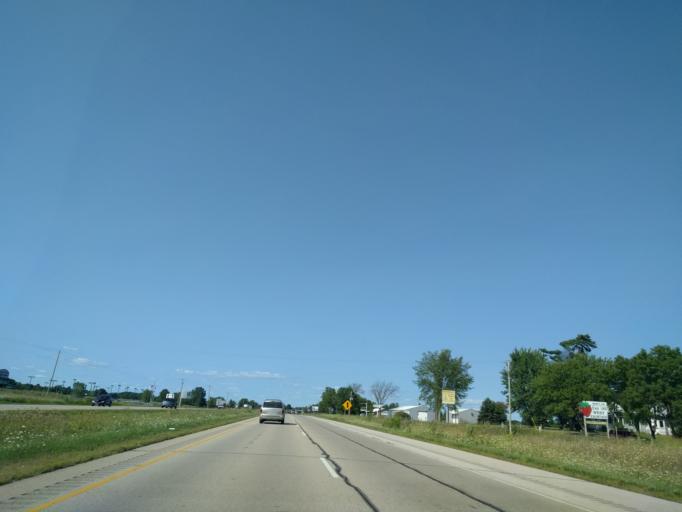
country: US
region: Wisconsin
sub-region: Brown County
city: Suamico
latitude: 44.7665
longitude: -88.0507
